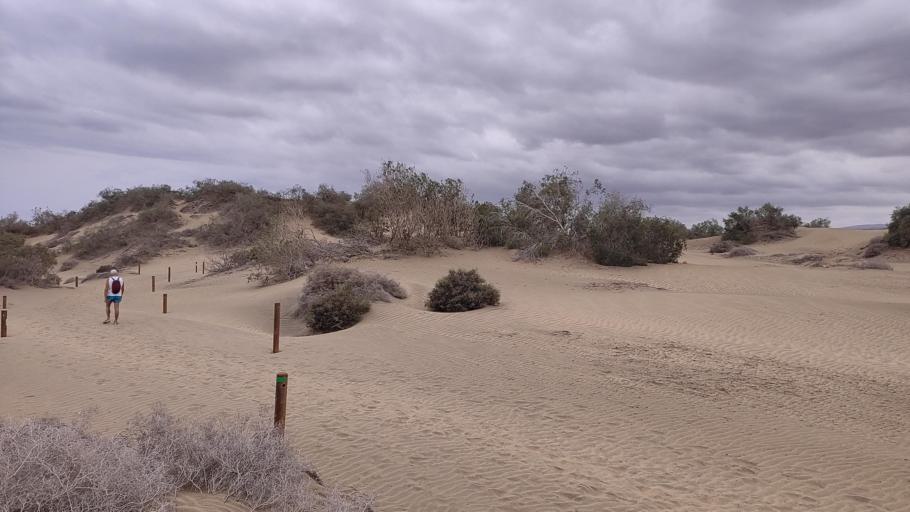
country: ES
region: Canary Islands
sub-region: Provincia de Las Palmas
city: Playa del Ingles
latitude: 27.7449
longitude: -15.5846
